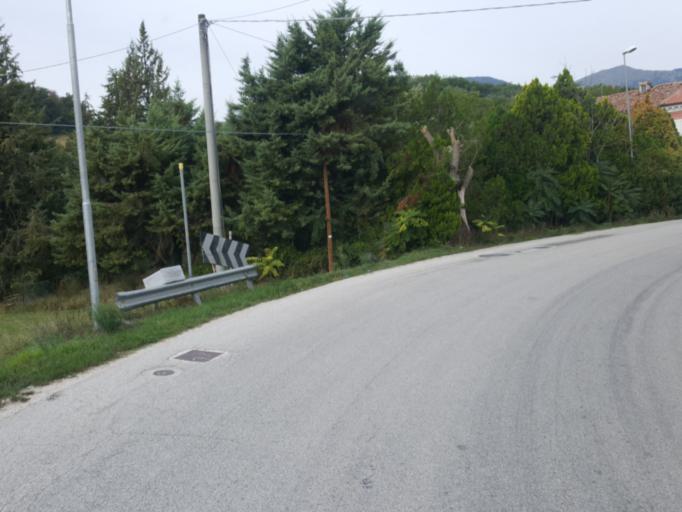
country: IT
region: The Marches
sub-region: Provincia di Ancona
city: Fabriano
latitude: 43.3455
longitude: 12.8486
